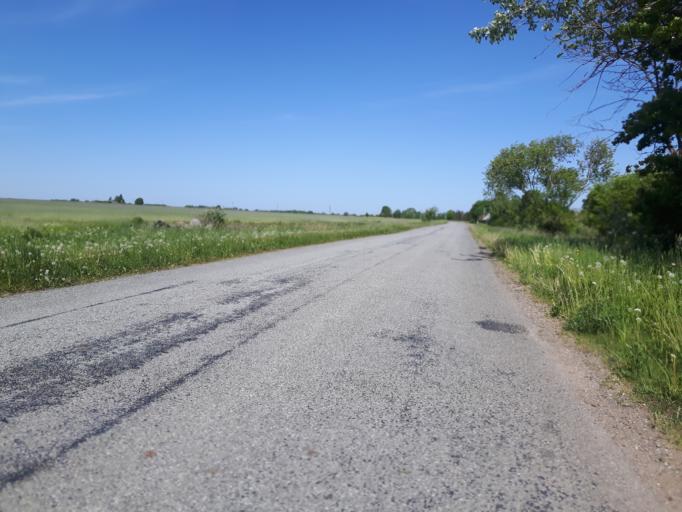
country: EE
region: Ida-Virumaa
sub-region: Aseri vald
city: Aseri
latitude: 59.4662
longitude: 26.8215
